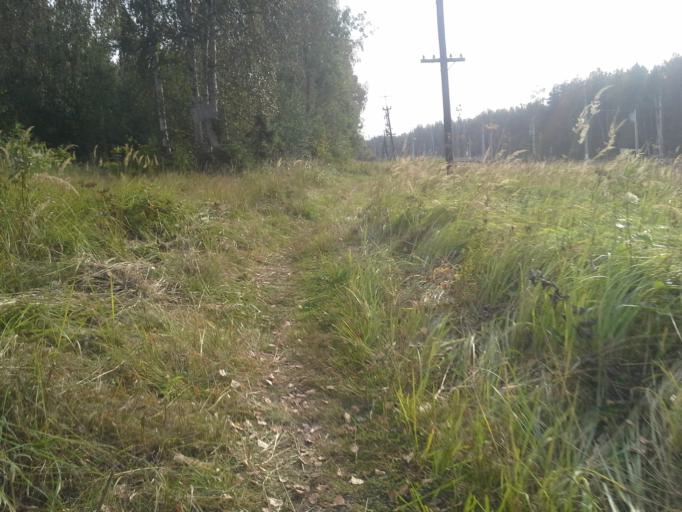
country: RU
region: Moskovskaya
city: Aprelevka
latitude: 55.5688
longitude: 37.0956
